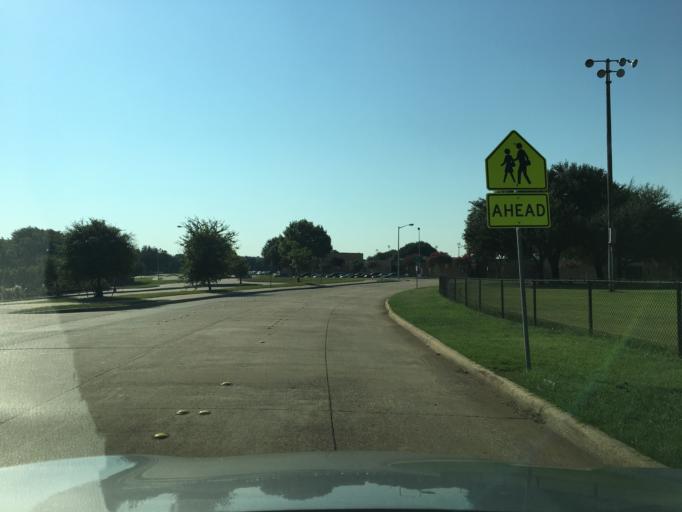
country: US
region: Texas
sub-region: Dallas County
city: Garland
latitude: 32.9562
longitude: -96.6516
